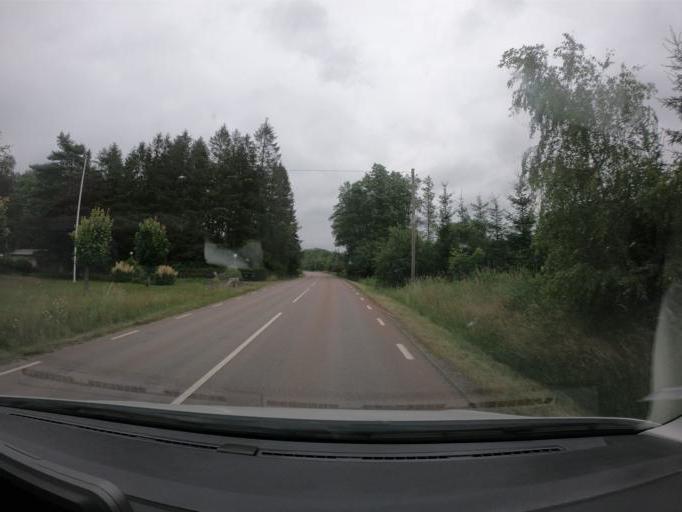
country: SE
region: Skane
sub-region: Perstorps Kommun
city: Perstorp
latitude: 56.1317
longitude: 13.3013
